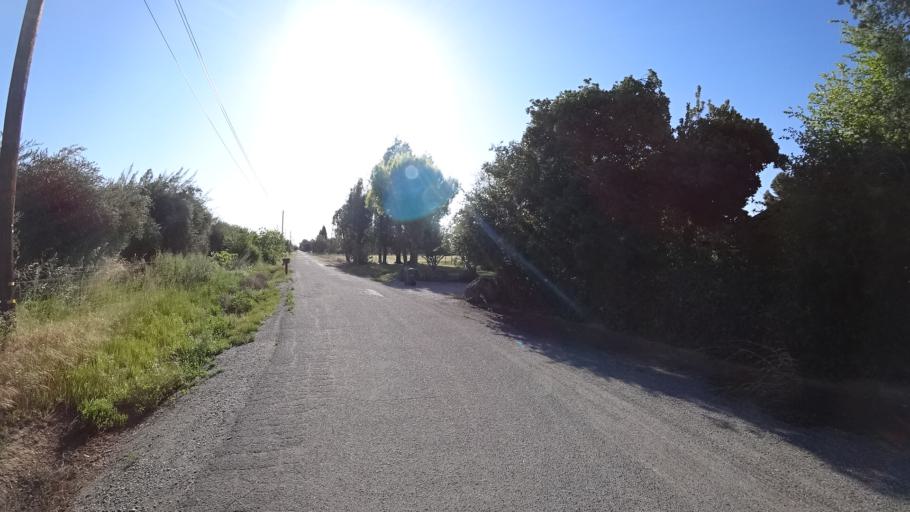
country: US
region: California
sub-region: Glenn County
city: Orland
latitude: 39.7220
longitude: -122.1876
